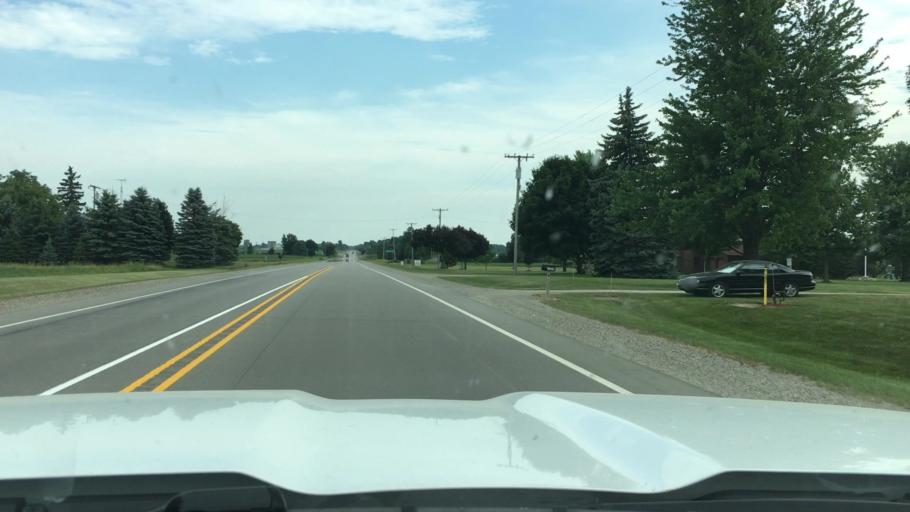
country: US
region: Michigan
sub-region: Sanilac County
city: Marlette
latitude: 43.3749
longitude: -83.0857
